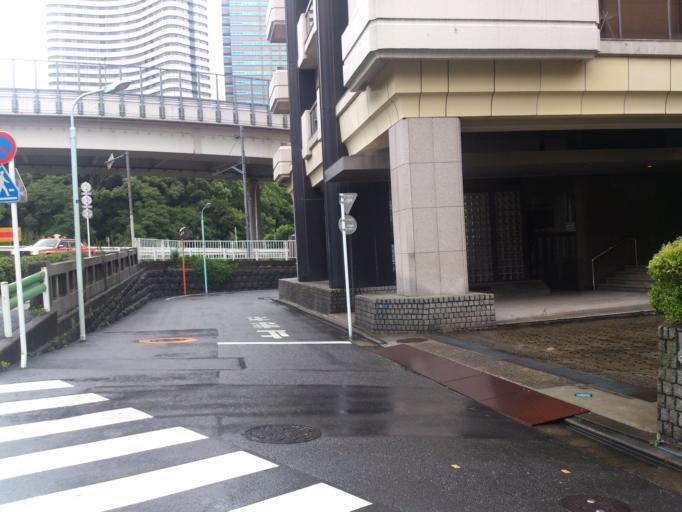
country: JP
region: Tokyo
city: Tokyo
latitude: 35.6787
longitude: 139.7325
